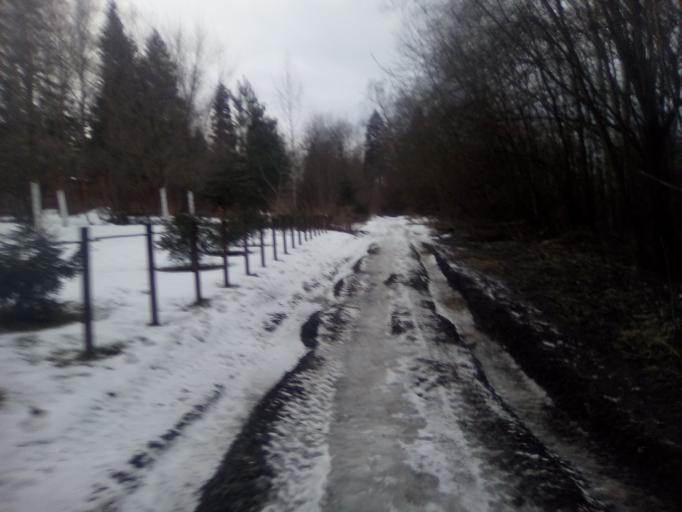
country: RU
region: Moskovskaya
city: Vatutinki
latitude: 55.5132
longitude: 37.3843
